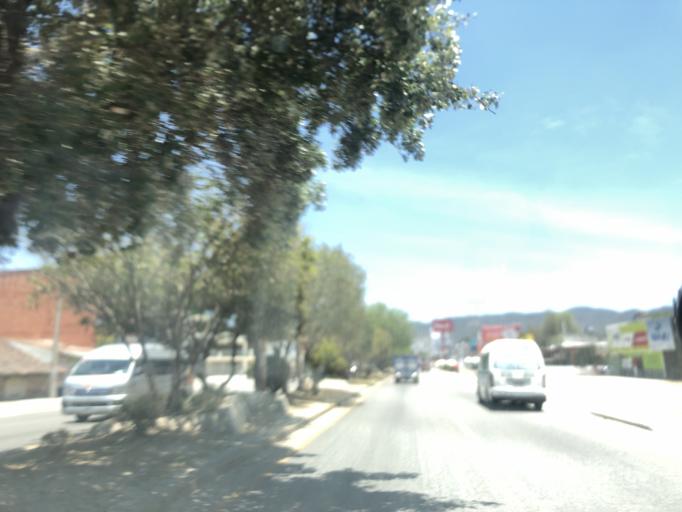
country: MX
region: Chiapas
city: San Cristobal de las Casas
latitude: 16.7238
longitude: -92.6347
